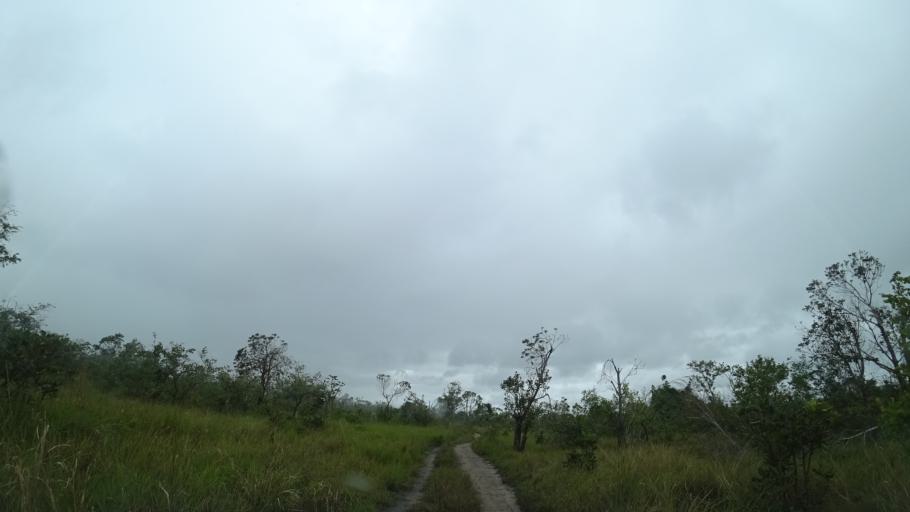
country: MZ
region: Sofala
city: Dondo
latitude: -19.5533
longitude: 35.0606
